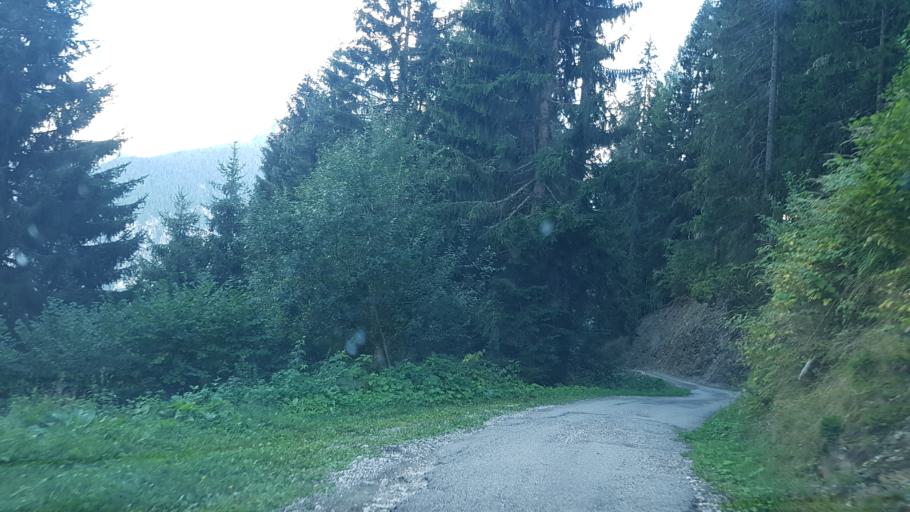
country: IT
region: Veneto
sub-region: Provincia di Belluno
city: San Pietro di Cadore
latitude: 46.5886
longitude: 12.5914
